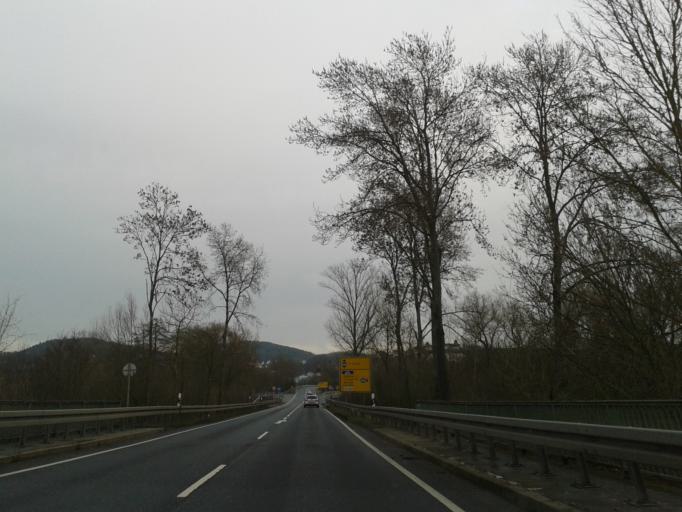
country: DE
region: Bavaria
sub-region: Upper Franconia
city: Ahorn
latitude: 50.2337
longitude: 10.9700
